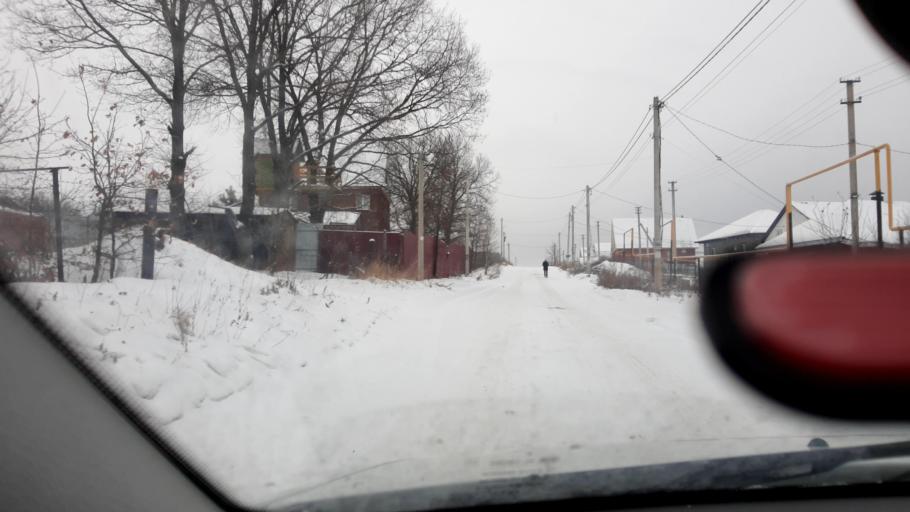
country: RU
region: Bashkortostan
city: Kabakovo
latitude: 54.6314
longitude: 56.0821
